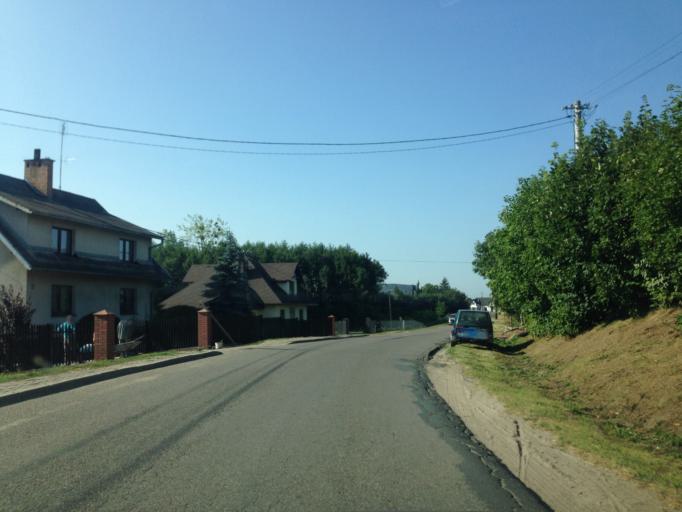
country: PL
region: Kujawsko-Pomorskie
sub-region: Powiat brodnicki
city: Brzozie
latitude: 53.3229
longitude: 19.5989
